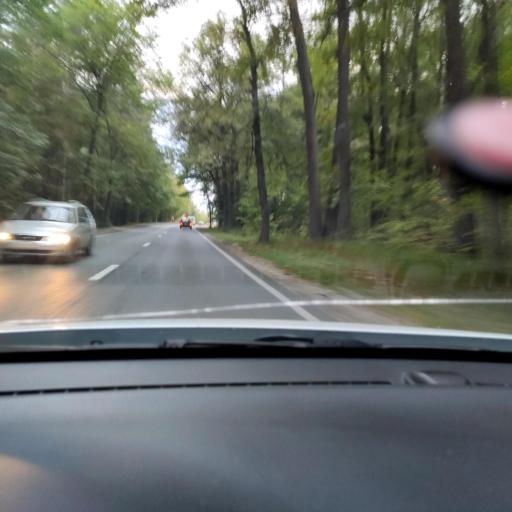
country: RU
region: Mariy-El
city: Volzhsk
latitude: 55.8450
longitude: 48.4087
